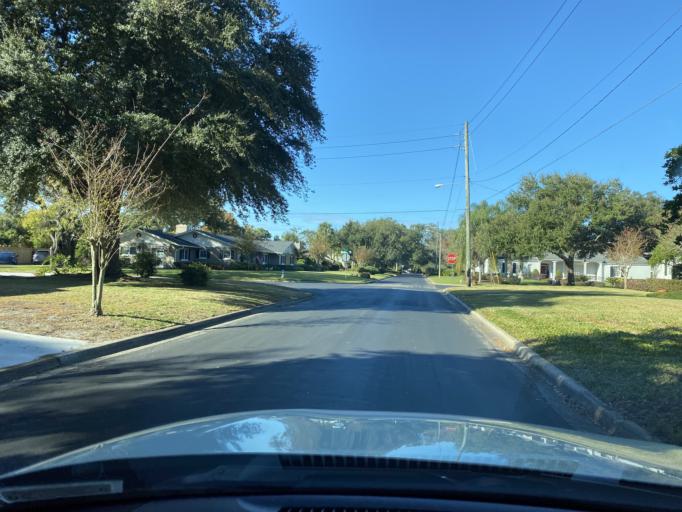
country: US
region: Florida
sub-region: Orange County
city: Orlando
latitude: 28.5547
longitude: -81.4023
